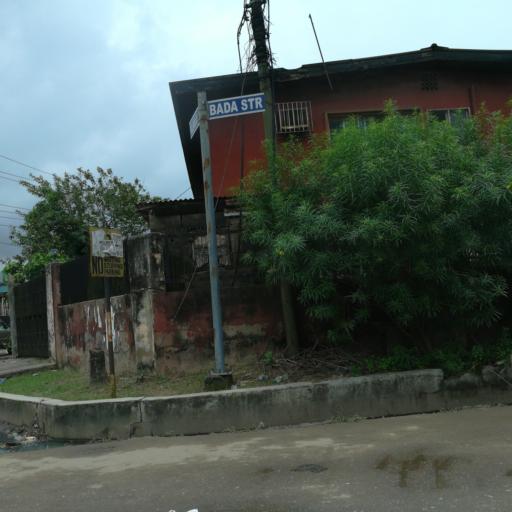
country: NG
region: Lagos
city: Agege
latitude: 6.6055
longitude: 3.3091
